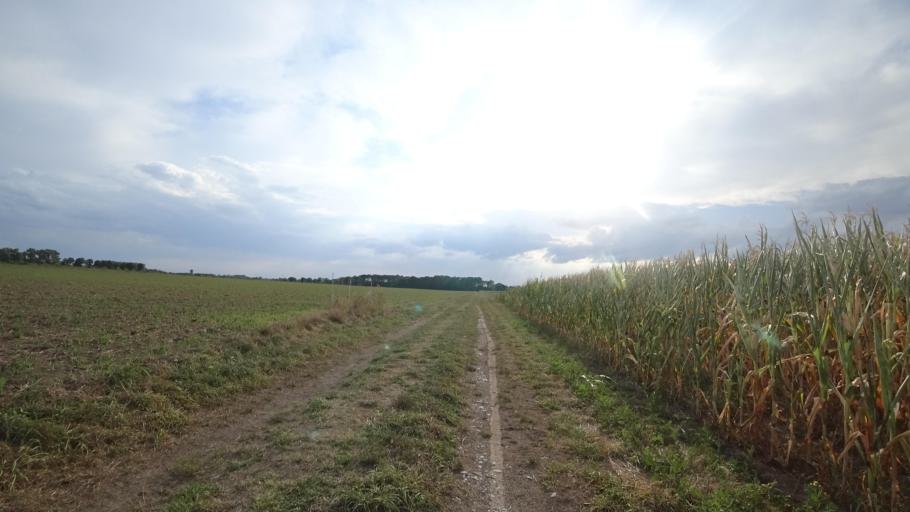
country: DE
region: North Rhine-Westphalia
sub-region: Regierungsbezirk Detmold
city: Rheda-Wiedenbruck
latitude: 51.8946
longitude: 8.3064
